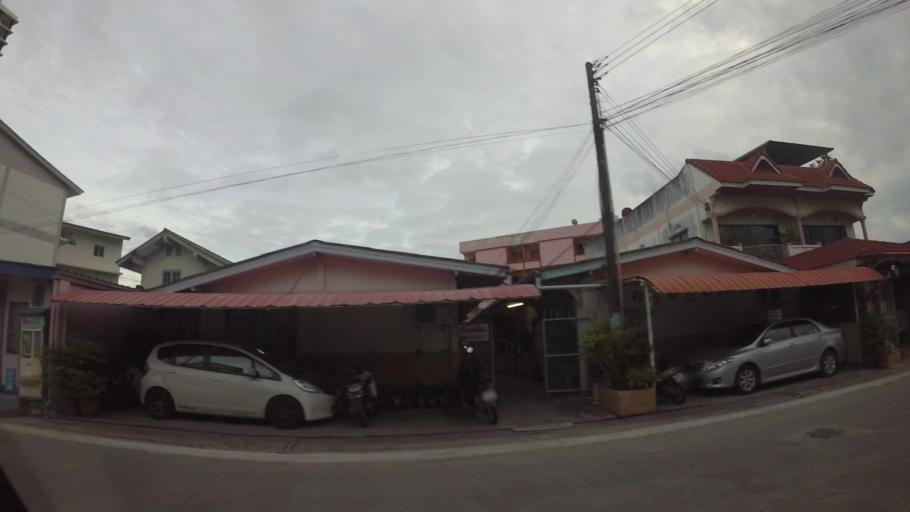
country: TH
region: Rayong
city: Rayong
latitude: 12.6712
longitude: 101.2677
